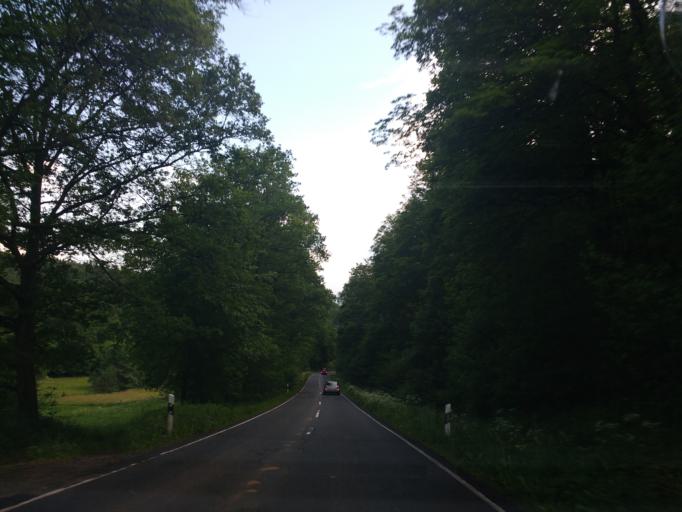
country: DE
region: Hesse
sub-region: Regierungsbezirk Giessen
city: Colbe
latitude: 50.9052
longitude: 8.8351
